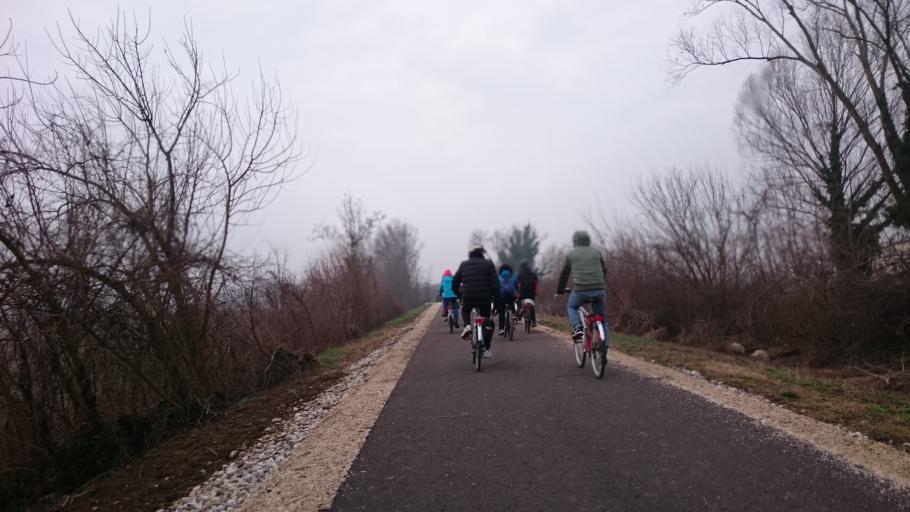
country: IT
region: Veneto
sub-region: Provincia di Vicenza
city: Grisignano di Zocco
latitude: 45.4814
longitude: 11.6783
